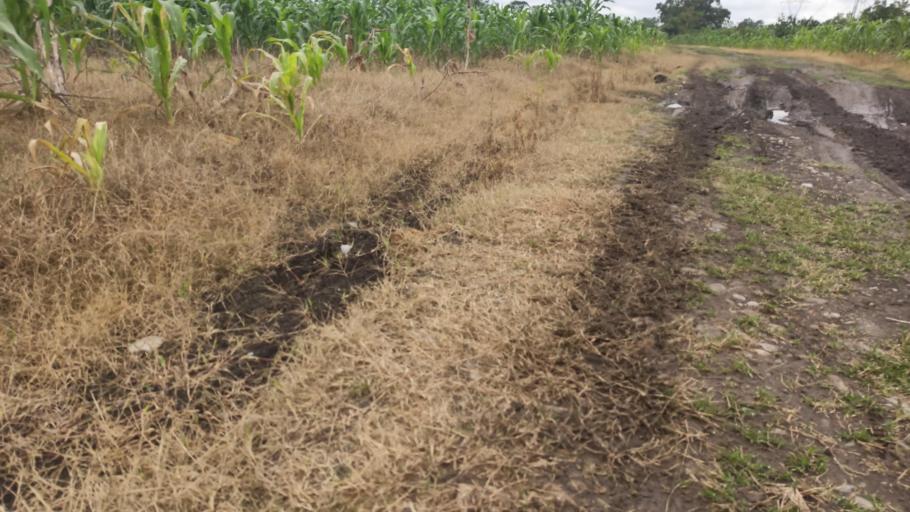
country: MX
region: Puebla
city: Espinal
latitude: 20.3046
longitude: -97.4118
